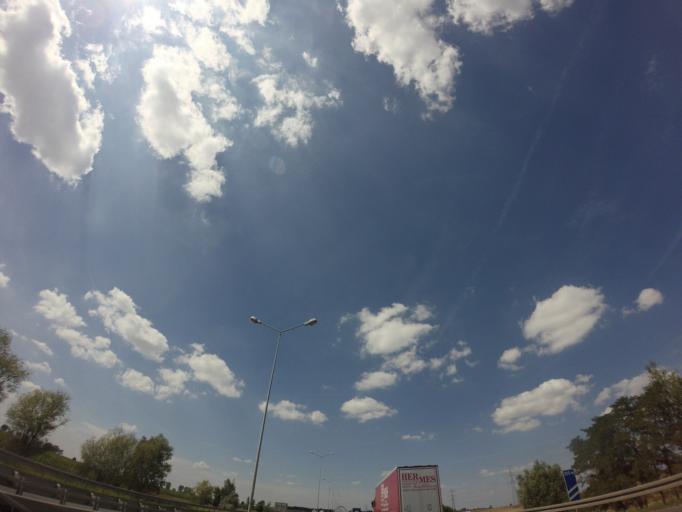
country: PL
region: Lower Silesian Voivodeship
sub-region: Powiat strzelinski
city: Wiazow
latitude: 50.8729
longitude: 17.2103
